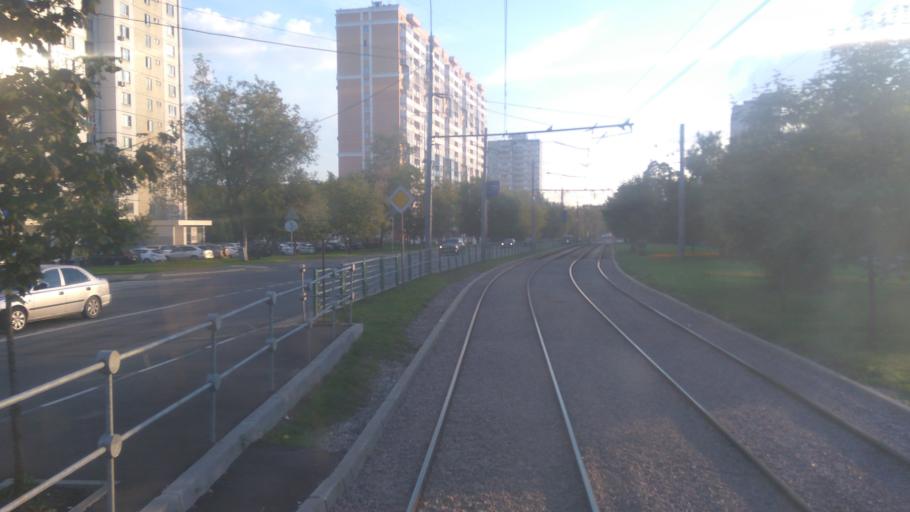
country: RU
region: Moscow
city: Metrogorodok
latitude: 55.8226
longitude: 37.7546
